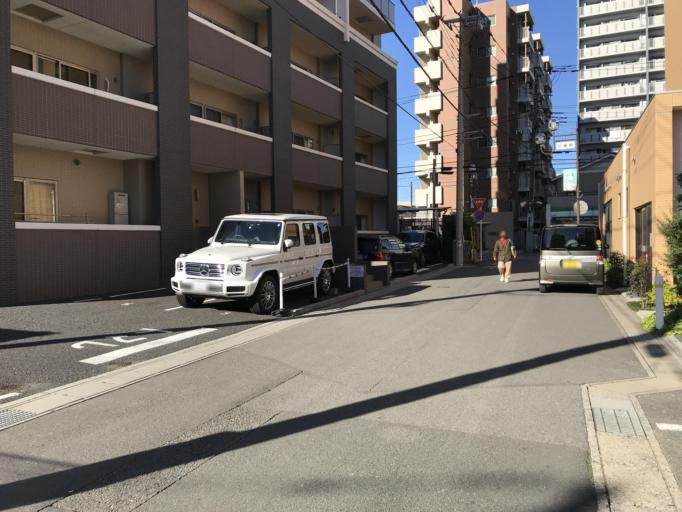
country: JP
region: Chiba
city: Nagareyama
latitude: 35.8276
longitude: 139.9306
